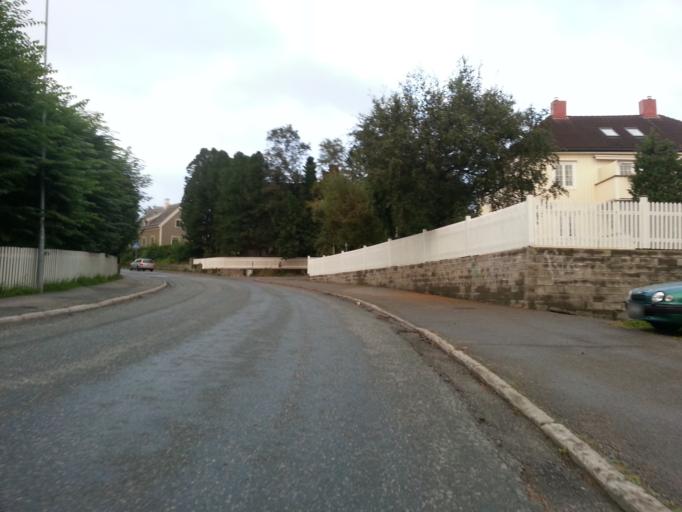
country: NO
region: Sor-Trondelag
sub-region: Trondheim
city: Trondheim
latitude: 63.4244
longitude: 10.4091
